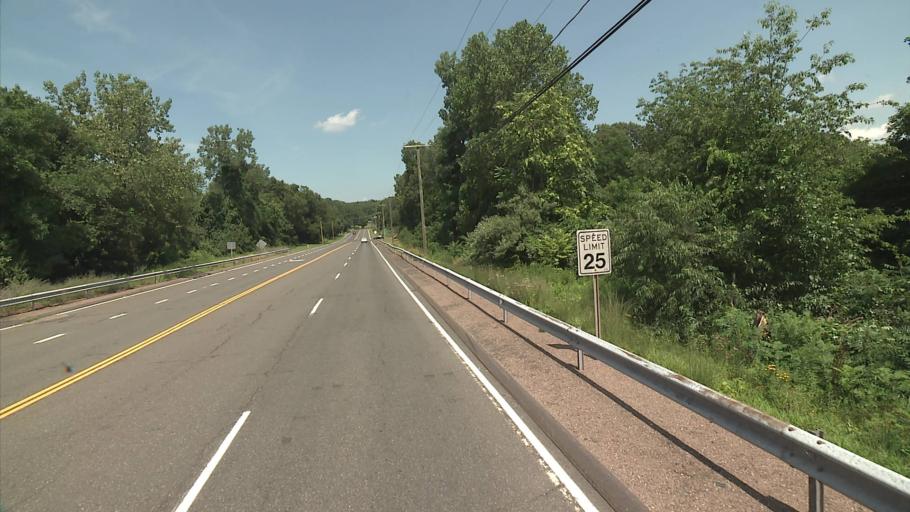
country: US
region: Connecticut
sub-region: Tolland County
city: Rockville
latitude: 41.8342
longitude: -72.4670
